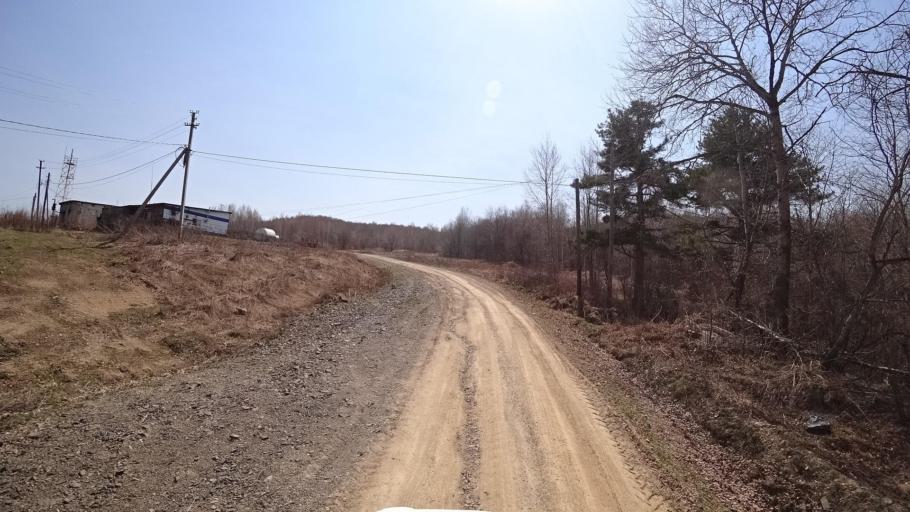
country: RU
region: Khabarovsk Krai
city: Selikhino
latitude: 50.6653
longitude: 137.4042
